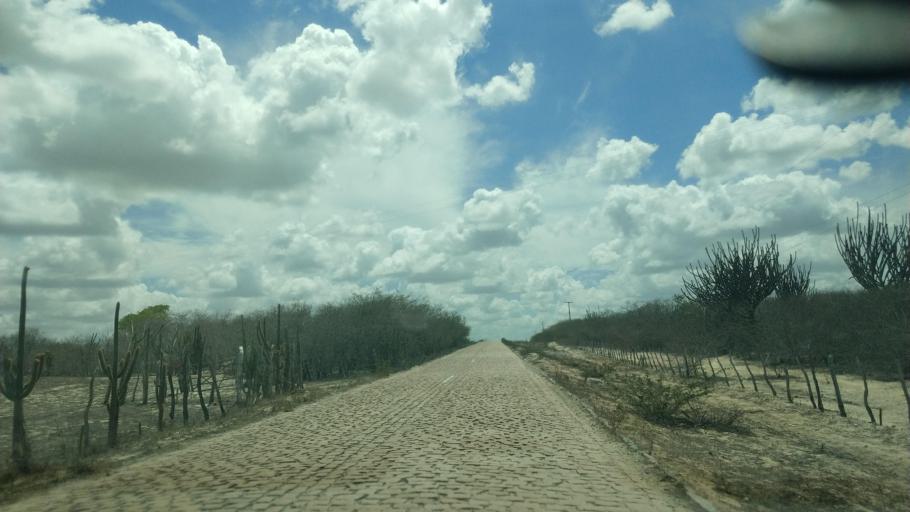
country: BR
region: Rio Grande do Norte
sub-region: Sao Paulo Do Potengi
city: Sao Paulo do Potengi
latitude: -5.9632
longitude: -35.8503
